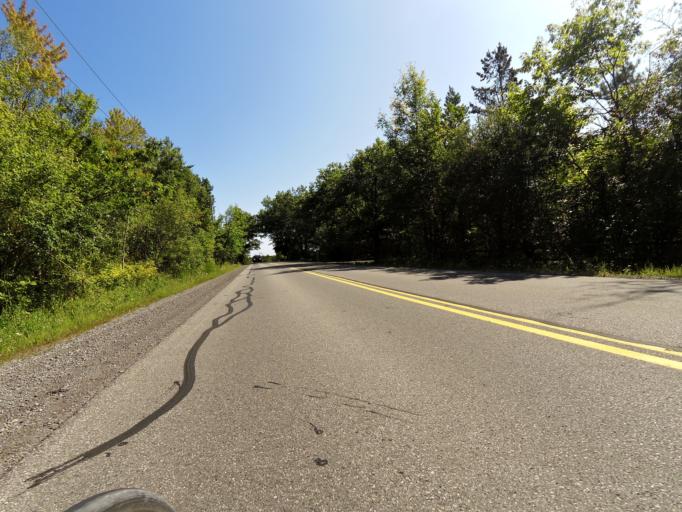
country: CA
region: Ontario
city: Bells Corners
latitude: 45.4042
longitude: -75.9255
